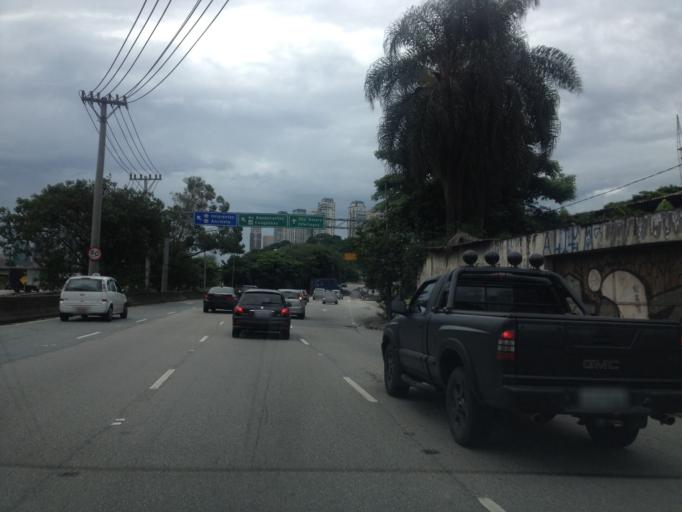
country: BR
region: Sao Paulo
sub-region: Sao Paulo
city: Sao Paulo
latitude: -23.5897
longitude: -46.6933
